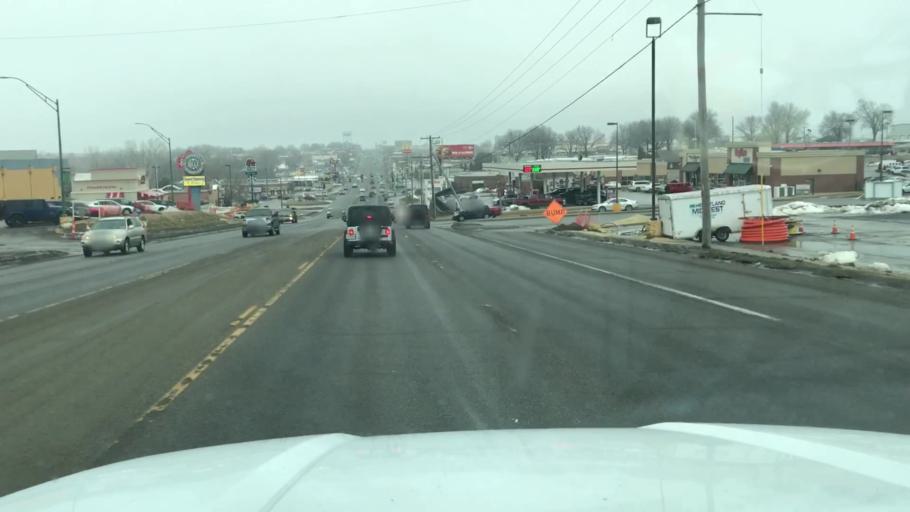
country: US
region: Missouri
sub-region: Buchanan County
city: Saint Joseph
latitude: 39.7669
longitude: -94.8036
